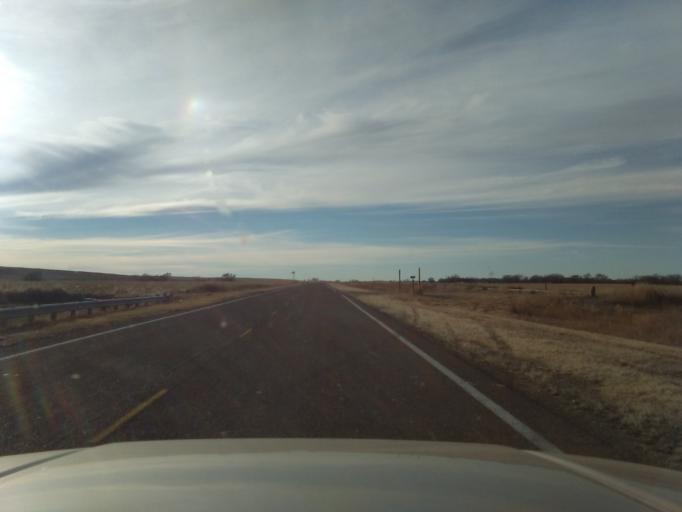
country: US
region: Kansas
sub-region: Norton County
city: Norton
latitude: 39.7561
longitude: -100.1188
